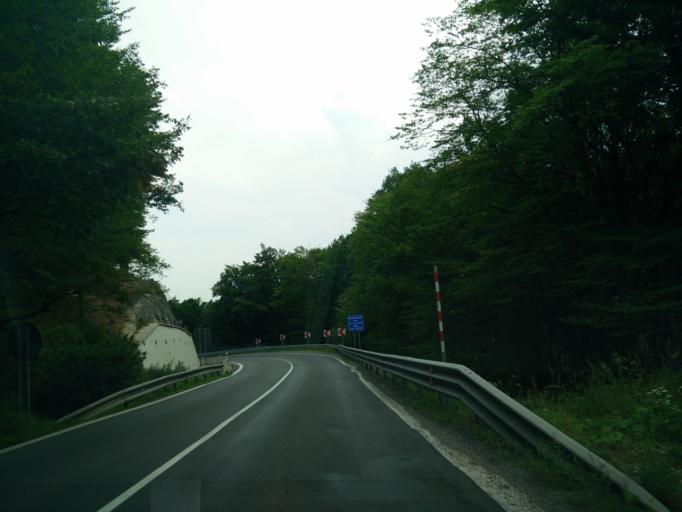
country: SK
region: Nitriansky
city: Handlova
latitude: 48.6580
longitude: 18.7348
